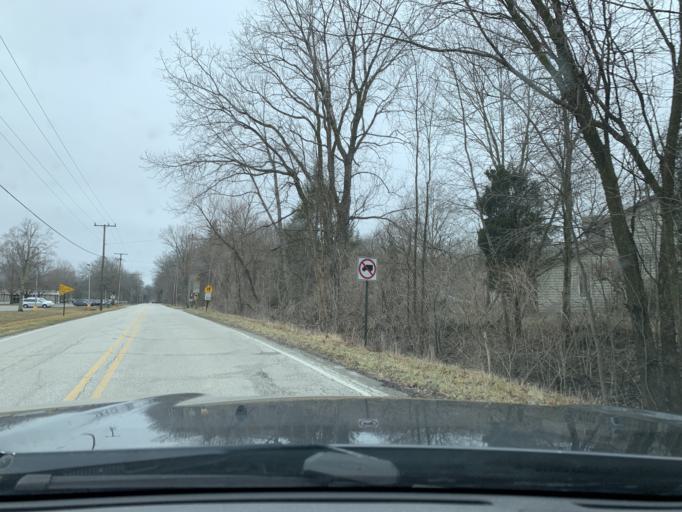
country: US
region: Indiana
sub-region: Porter County
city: Chesterton
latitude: 41.6171
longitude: -87.0165
